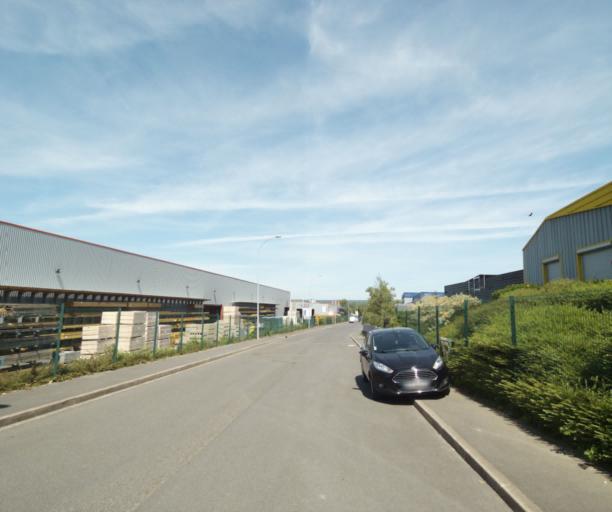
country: FR
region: Champagne-Ardenne
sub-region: Departement des Ardennes
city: Charleville-Mezieres
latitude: 49.7528
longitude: 4.7099
